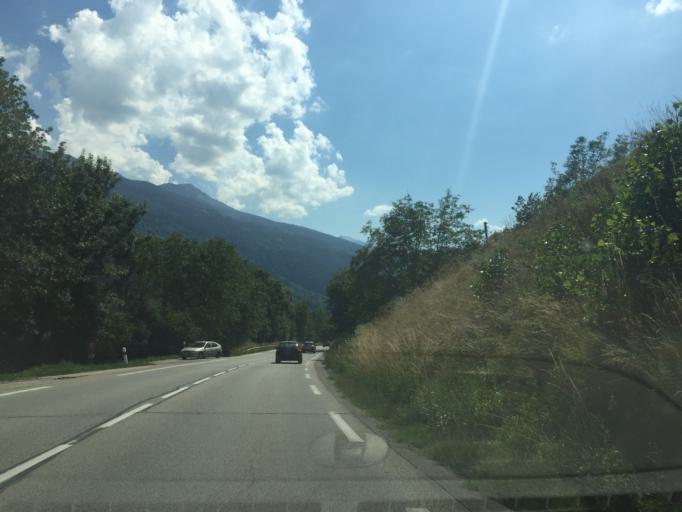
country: FR
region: Rhone-Alpes
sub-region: Departement de la Savoie
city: Bourg-Saint-Maurice
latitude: 45.5806
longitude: 6.7369
